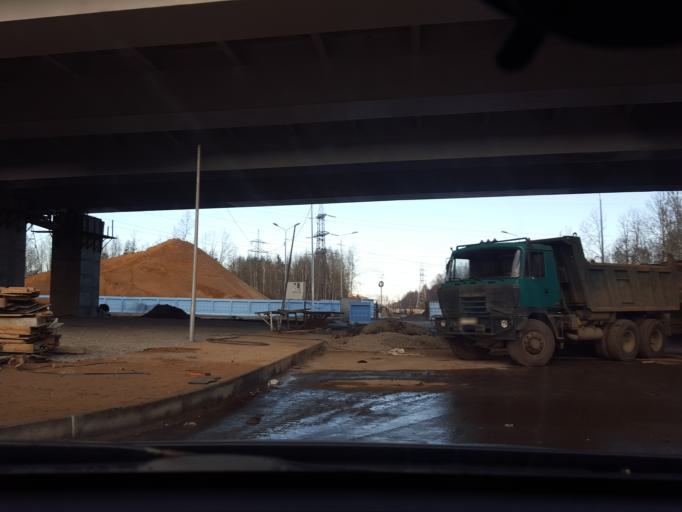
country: RU
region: St.-Petersburg
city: Shuvalovo
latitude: 60.0610
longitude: 30.2815
